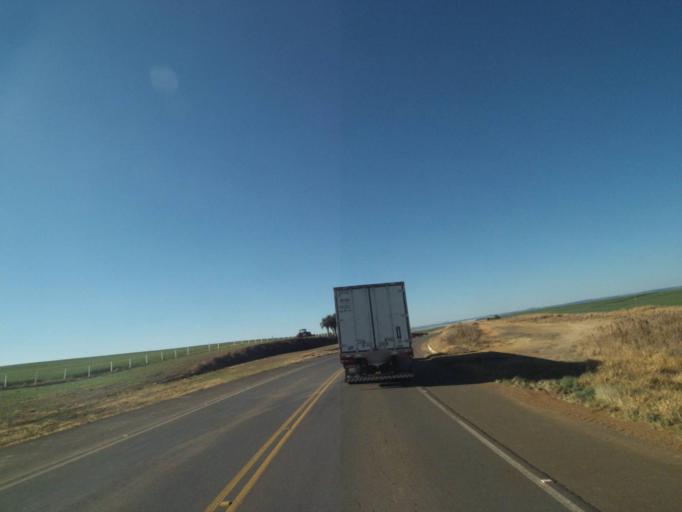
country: BR
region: Parana
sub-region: Tibagi
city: Tibagi
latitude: -24.6330
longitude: -50.4599
